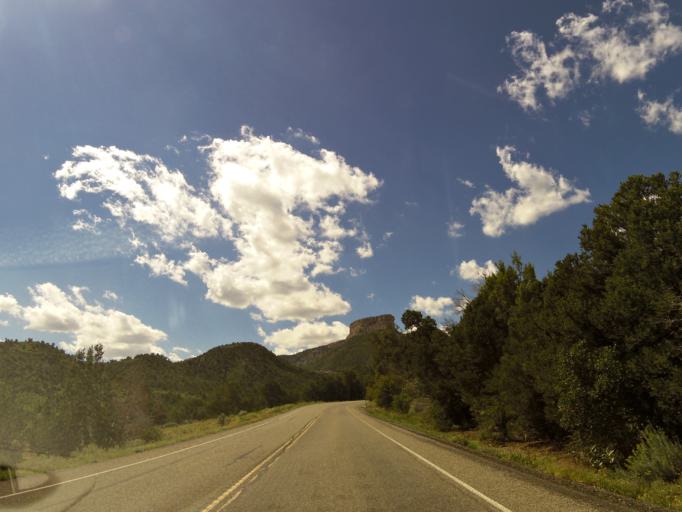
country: US
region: Colorado
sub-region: Montezuma County
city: Mancos
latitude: 37.3348
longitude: -108.4120
